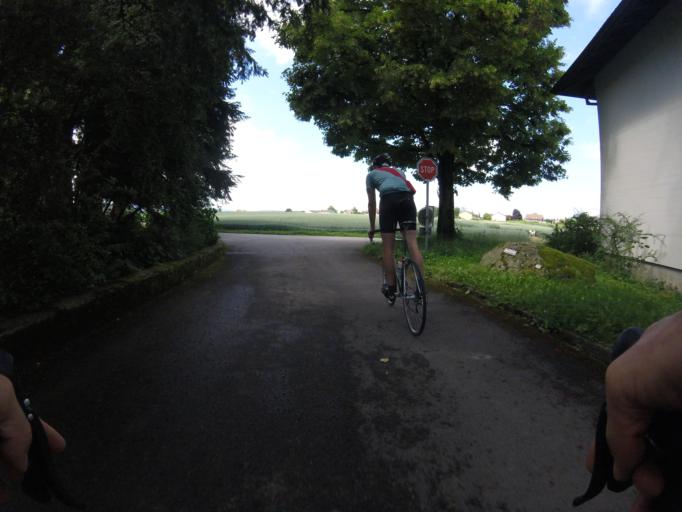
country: CH
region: Bern
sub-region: Bern-Mittelland District
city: Zollikofen
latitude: 46.9880
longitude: 7.4621
